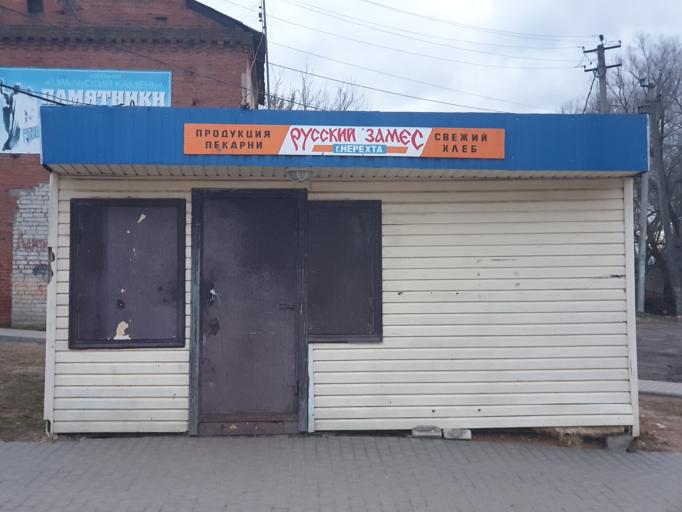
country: RU
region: Kostroma
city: Nerekhta
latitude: 57.4612
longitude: 40.5712
